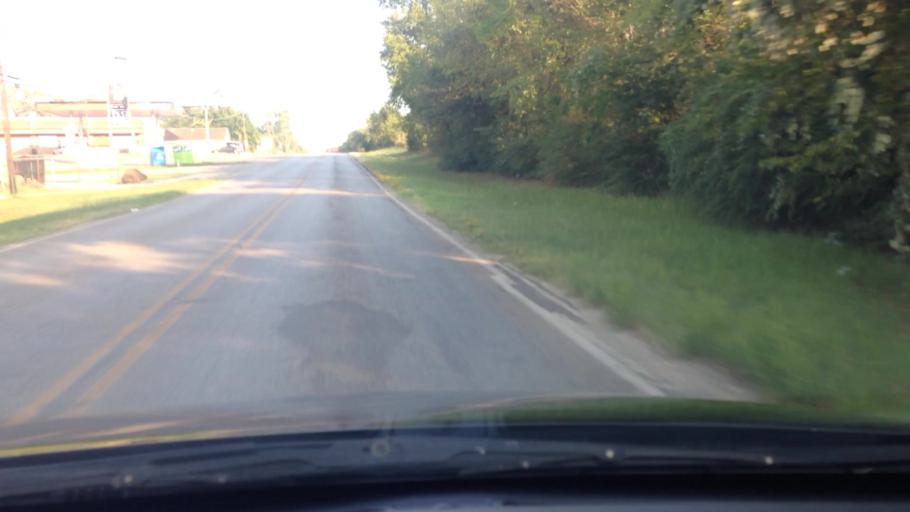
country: US
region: Texas
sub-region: Tarrant County
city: Rendon
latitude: 32.5861
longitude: -97.2459
